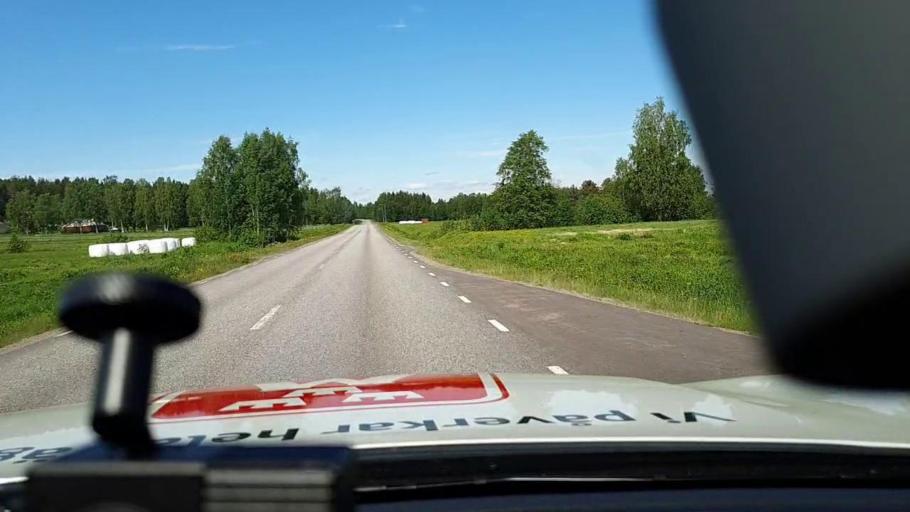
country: SE
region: Norrbotten
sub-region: Lulea Kommun
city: Sodra Sunderbyn
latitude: 65.6558
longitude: 21.8495
